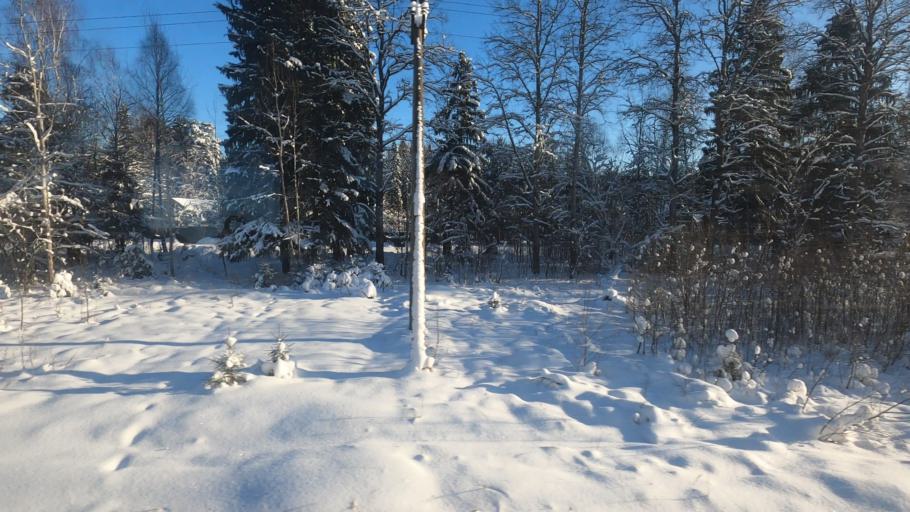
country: RU
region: Moskovskaya
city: Novo-Nikol'skoye
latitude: 56.5478
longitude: 37.5604
